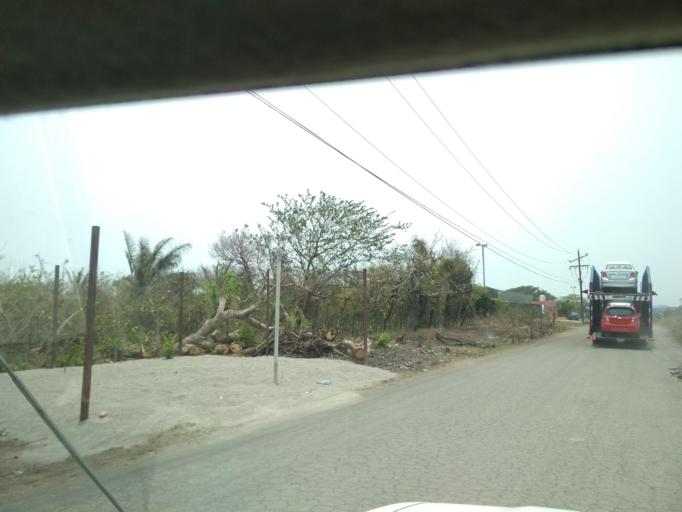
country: MX
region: Veracruz
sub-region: Veracruz
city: Delfino Victoria (Santa Fe)
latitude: 19.2017
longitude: -96.2664
